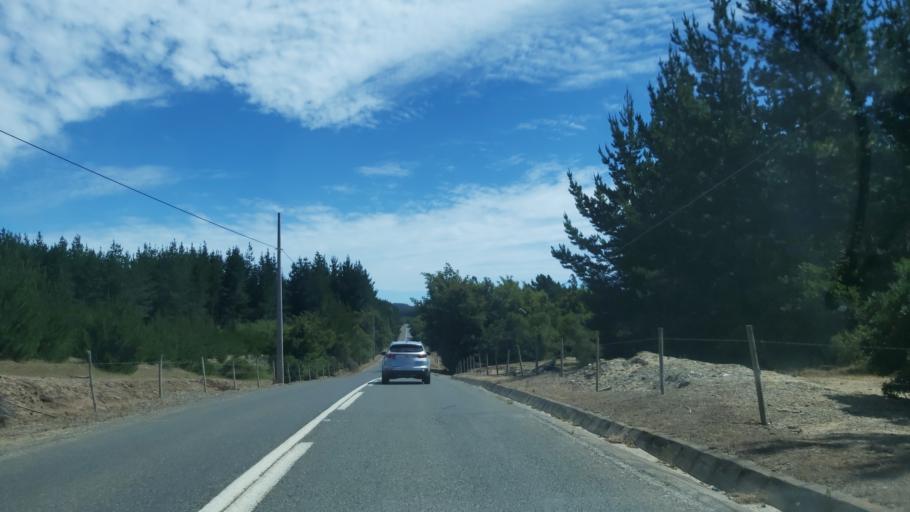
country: CL
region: Maule
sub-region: Provincia de Talca
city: Constitucion
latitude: -35.5242
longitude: -72.5373
